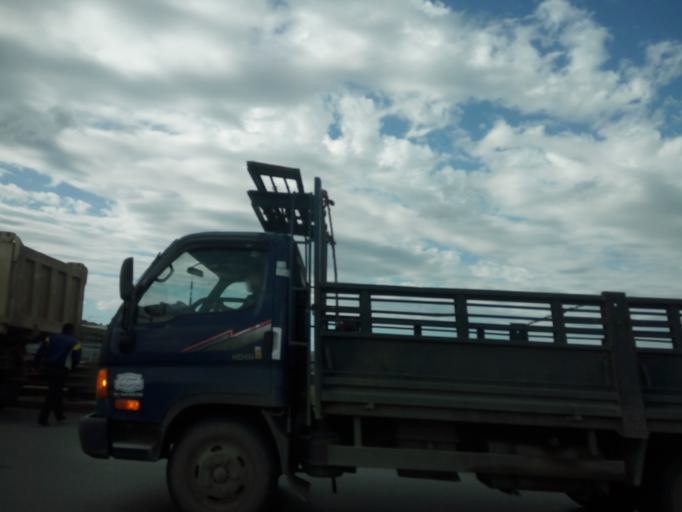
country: DZ
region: Tipaza
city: El Affroun
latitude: 36.4475
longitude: 2.6464
